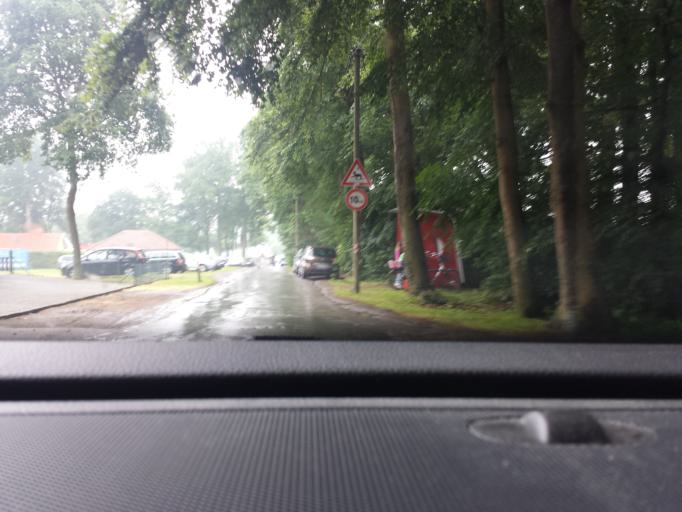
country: DE
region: North Rhine-Westphalia
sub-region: Regierungsbezirk Munster
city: Gronau
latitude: 52.1926
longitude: 7.0565
